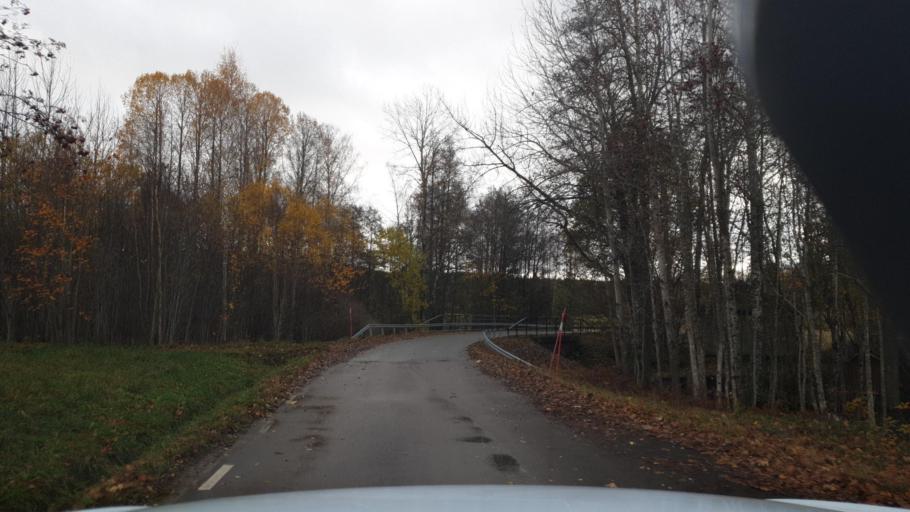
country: SE
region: Vaermland
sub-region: Arvika Kommun
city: Arvika
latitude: 59.5305
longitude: 12.7417
